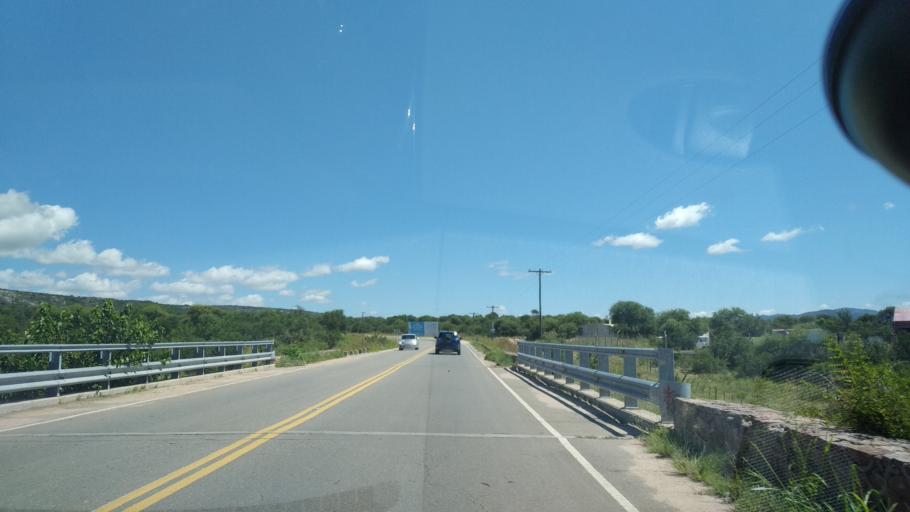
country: AR
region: Cordoba
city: Villa Cura Brochero
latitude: -31.6992
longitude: -65.0374
